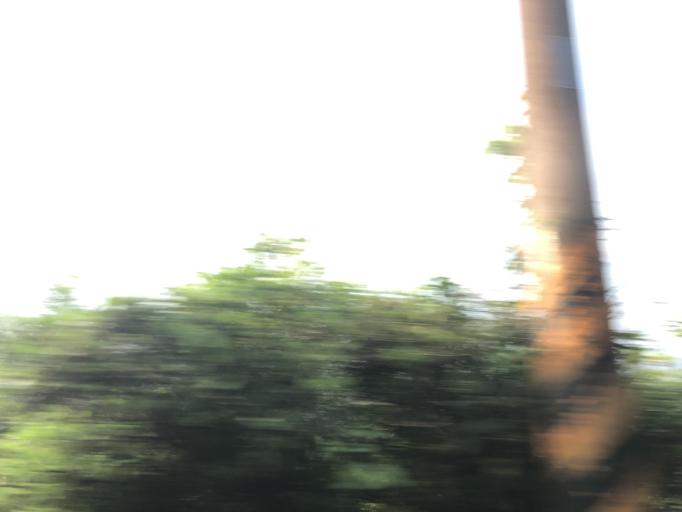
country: TW
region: Taiwan
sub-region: Keelung
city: Keelung
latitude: 25.1502
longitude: 121.6314
